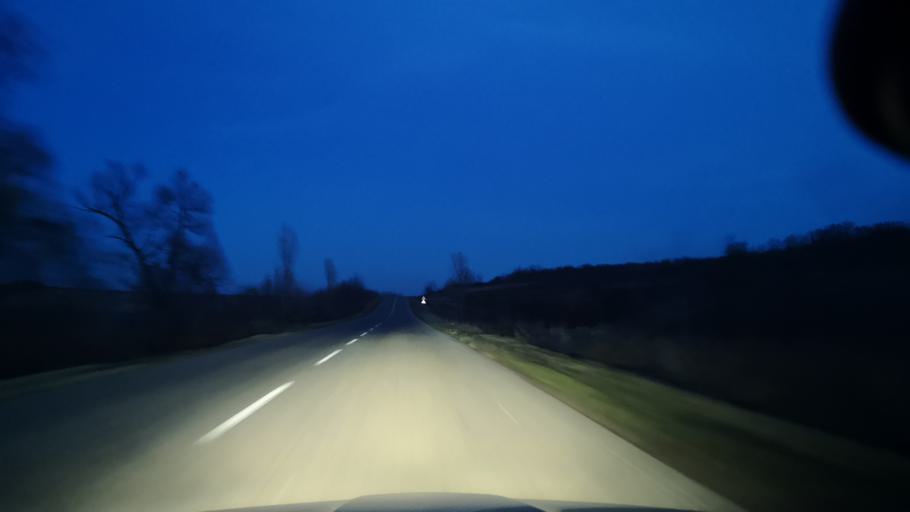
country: MD
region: Orhei
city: Orhei
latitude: 47.3445
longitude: 28.7150
